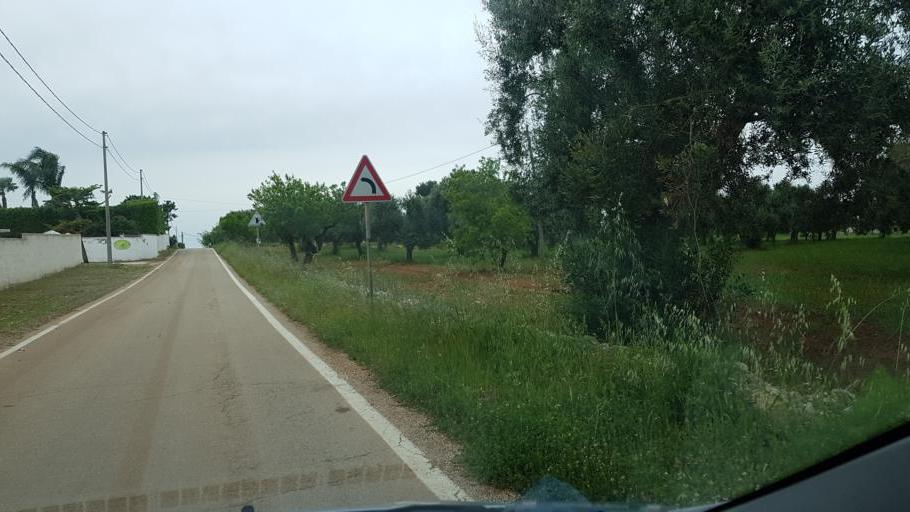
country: IT
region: Apulia
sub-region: Provincia di Brindisi
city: San Vito dei Normanni
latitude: 40.6688
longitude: 17.7591
